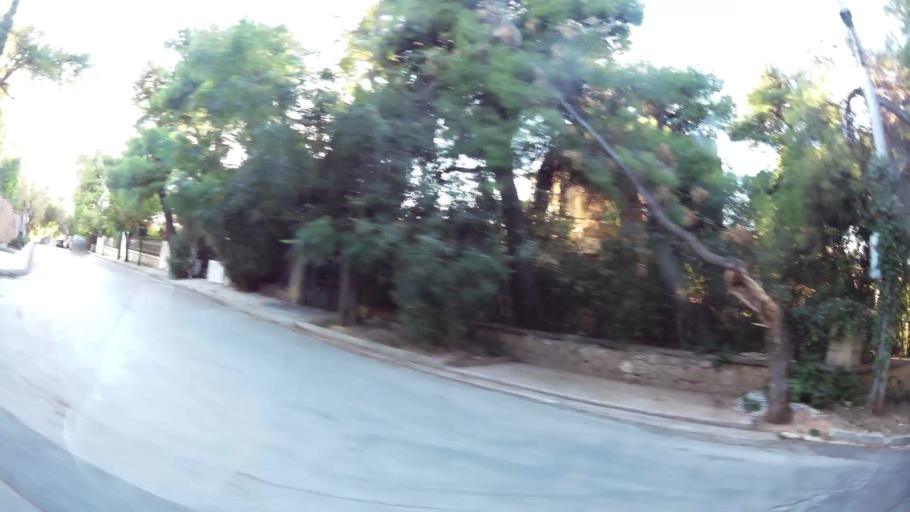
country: GR
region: Attica
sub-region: Nomarchia Athinas
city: Nea Erythraia
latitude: 38.0909
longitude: 23.8250
